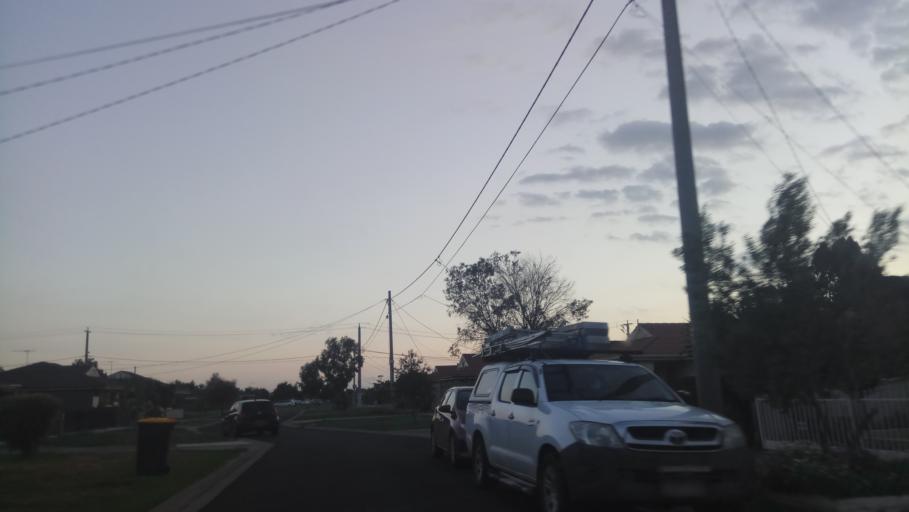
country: AU
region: Victoria
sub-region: Hobsons Bay
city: Altona Meadows
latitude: -37.8762
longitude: 144.7780
